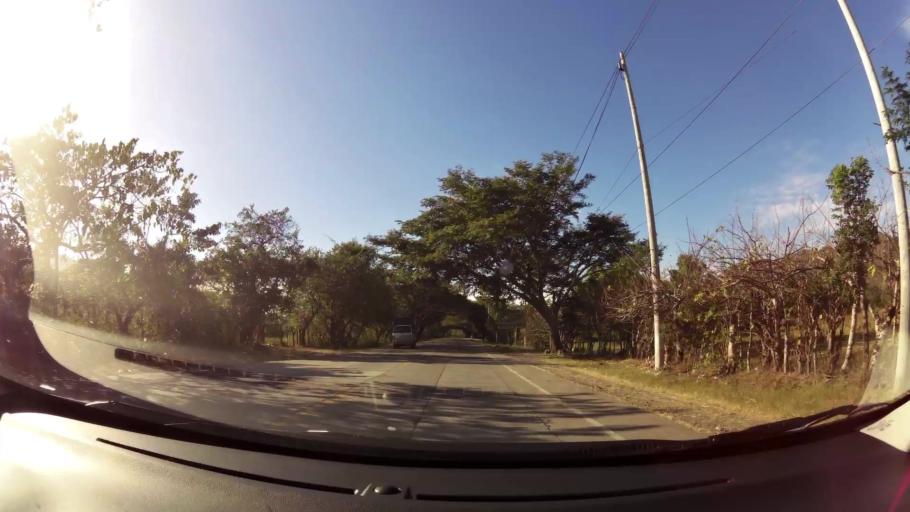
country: SV
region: Santa Ana
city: Texistepeque
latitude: 14.1317
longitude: -89.5039
